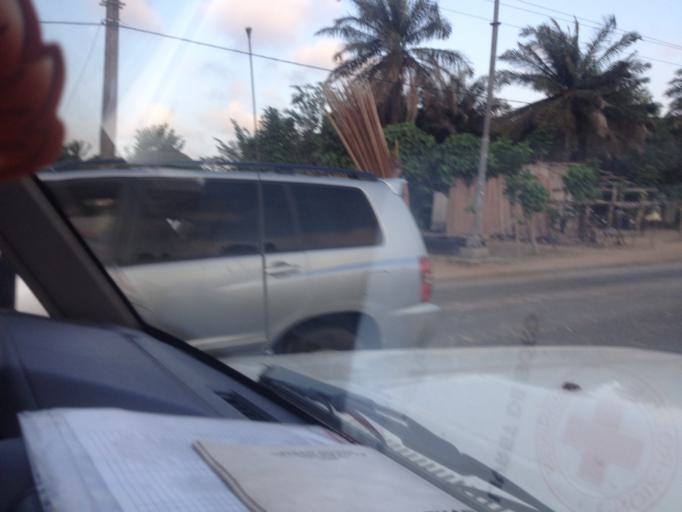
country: BJ
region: Queme
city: Porto-Novo
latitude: 6.4194
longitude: 2.6280
